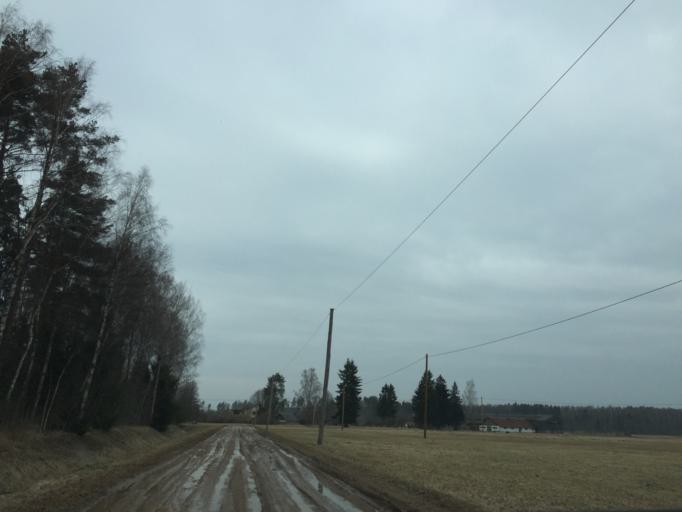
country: LV
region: Ozolnieku
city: Ozolnieki
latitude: 56.7219
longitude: 23.8428
